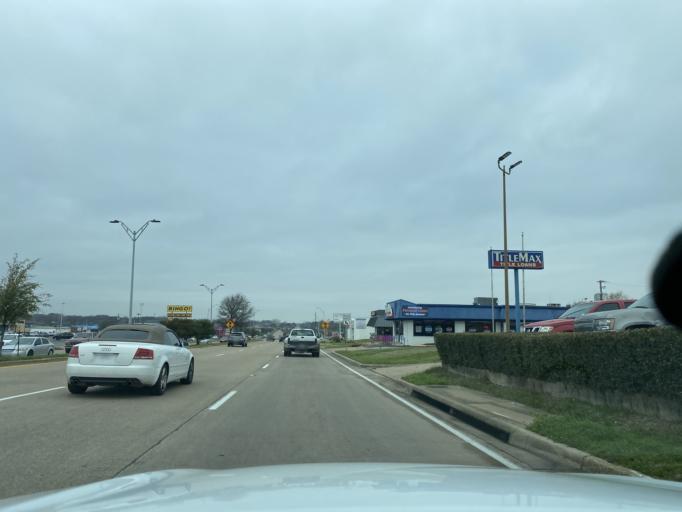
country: US
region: Texas
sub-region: Tarrant County
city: Arlington
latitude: 32.7081
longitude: -97.0944
